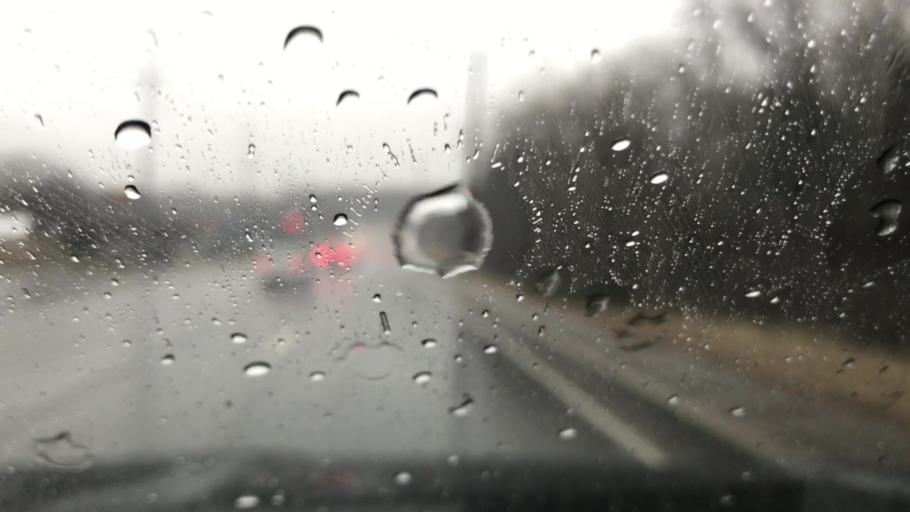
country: US
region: Tennessee
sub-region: Williamson County
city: Nolensville
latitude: 36.0466
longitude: -86.6782
